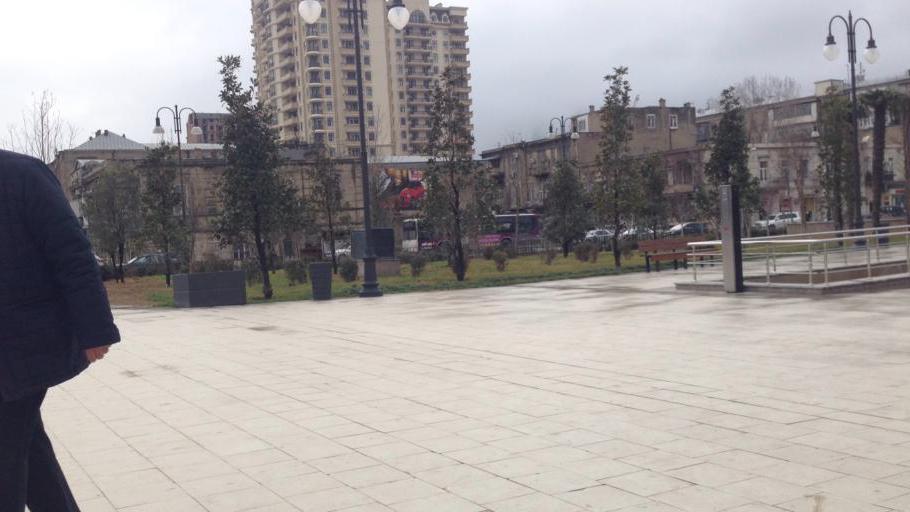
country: AZ
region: Baki
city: Badamdar
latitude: 40.3758
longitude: 49.8338
